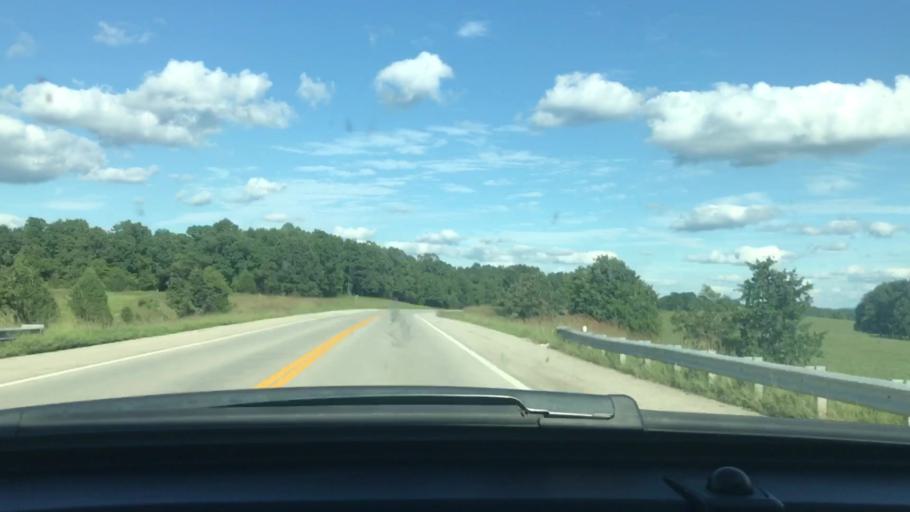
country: US
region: Missouri
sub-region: Howell County
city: West Plains
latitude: 36.6609
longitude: -91.7135
